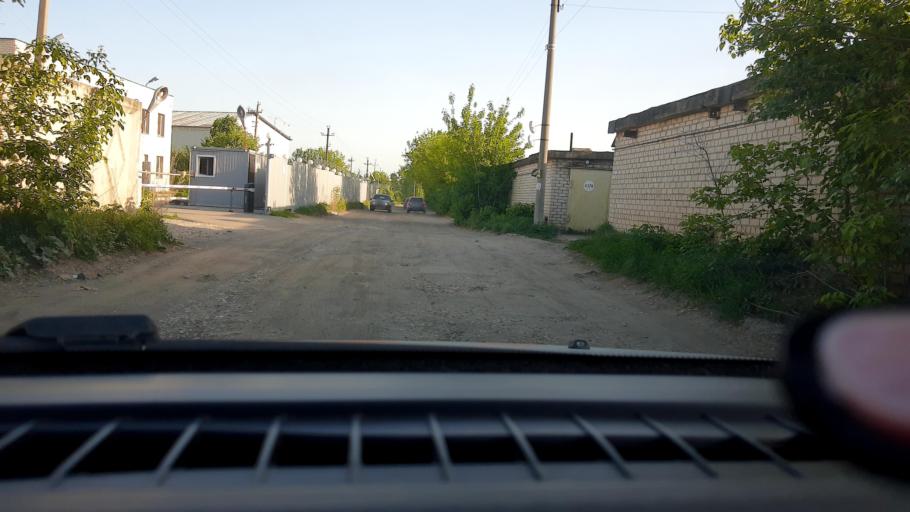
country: RU
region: Nizjnij Novgorod
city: Kstovo
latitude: 56.1355
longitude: 44.1916
